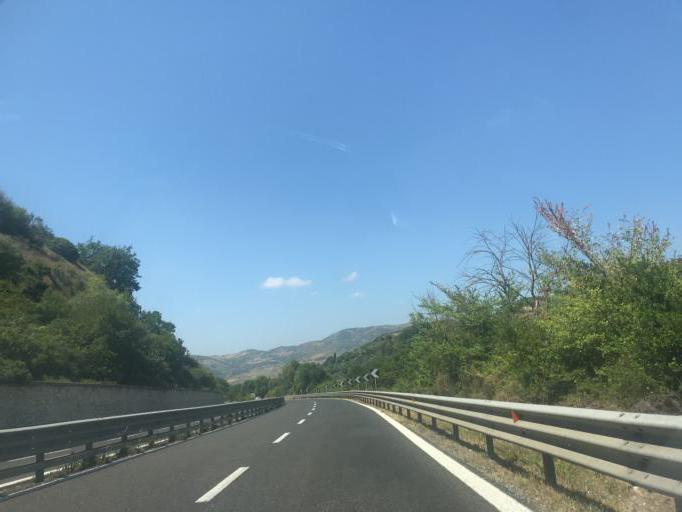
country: IT
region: Sardinia
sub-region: Provincia di Sassari
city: Codrongianos
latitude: 40.6579
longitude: 8.6716
